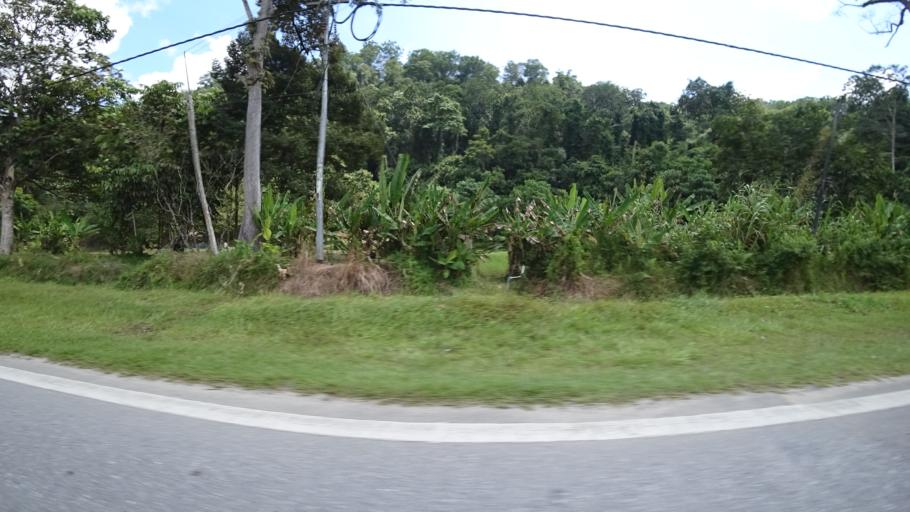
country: MY
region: Sarawak
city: Limbang
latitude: 4.6877
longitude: 114.9818
